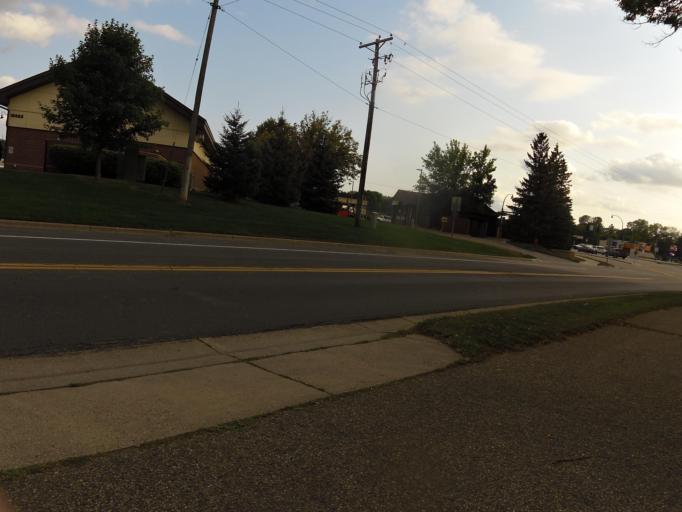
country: US
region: Minnesota
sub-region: Scott County
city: Prior Lake
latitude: 44.7084
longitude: -93.4336
